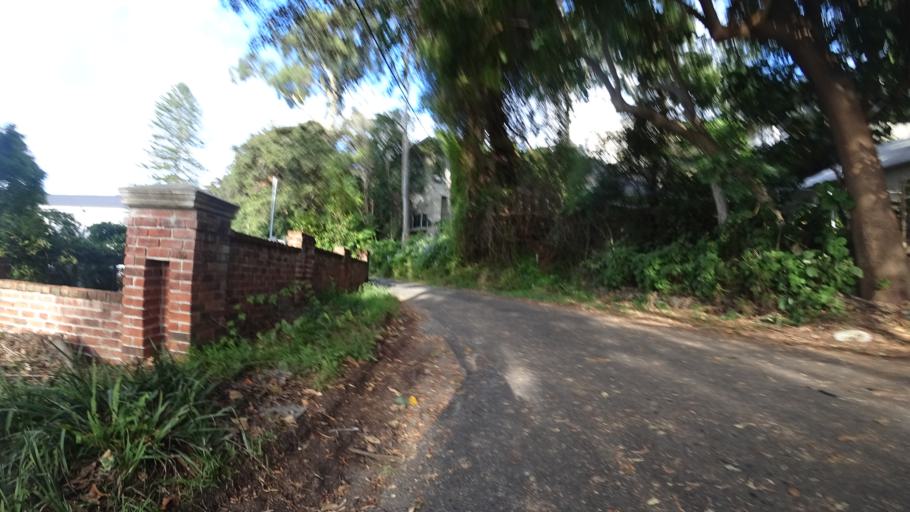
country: AU
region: New South Wales
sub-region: Hunters Hill
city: Hunters Hill
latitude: -33.8322
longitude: 151.1504
